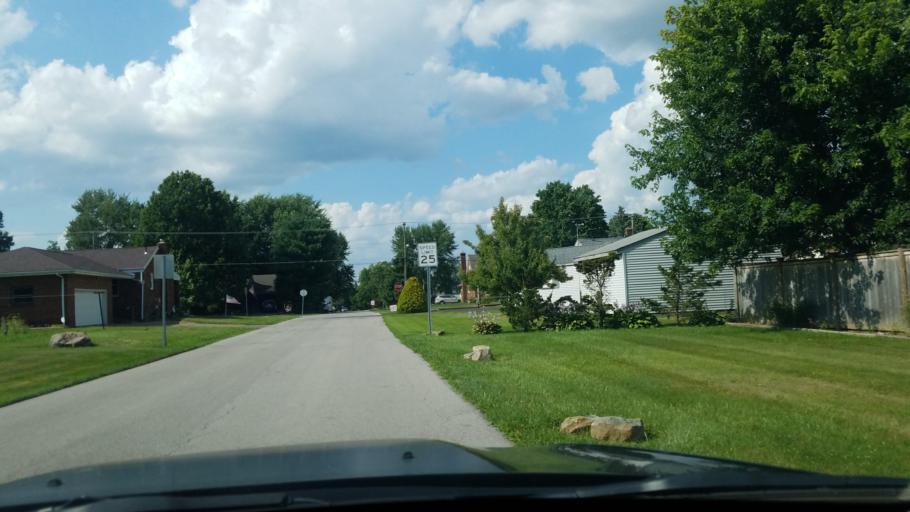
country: US
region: Ohio
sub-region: Mahoning County
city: Struthers
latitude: 41.0421
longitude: -80.6113
